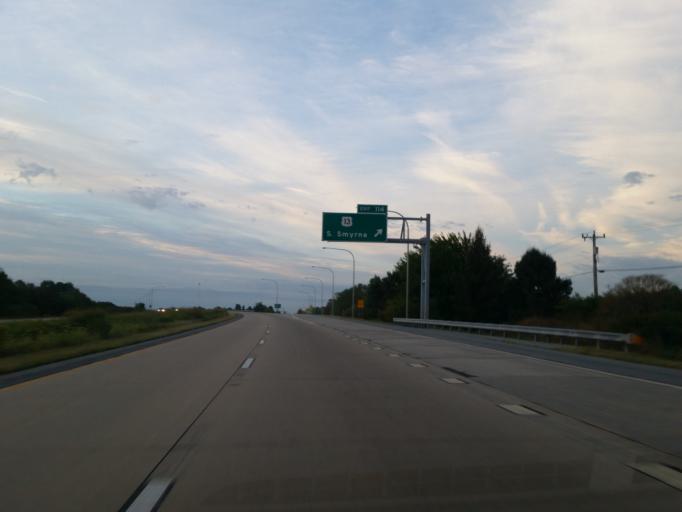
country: US
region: Delaware
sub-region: Kent County
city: Smyrna
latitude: 39.2880
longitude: -75.5929
